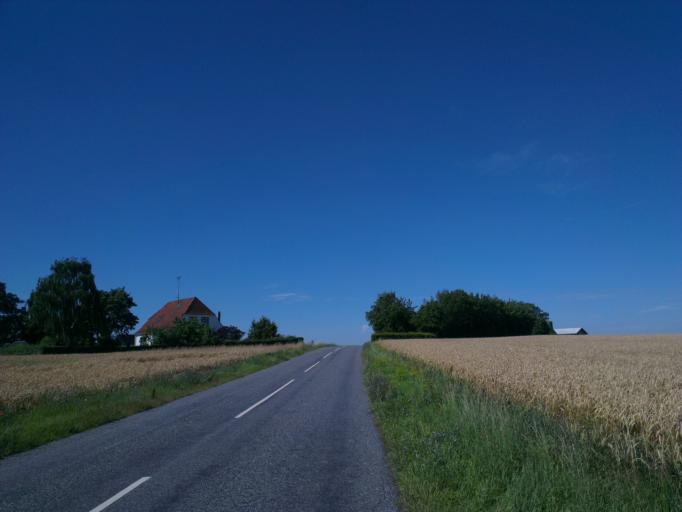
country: DK
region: Capital Region
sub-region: Frederikssund Kommune
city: Frederikssund
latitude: 55.8657
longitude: 12.0919
